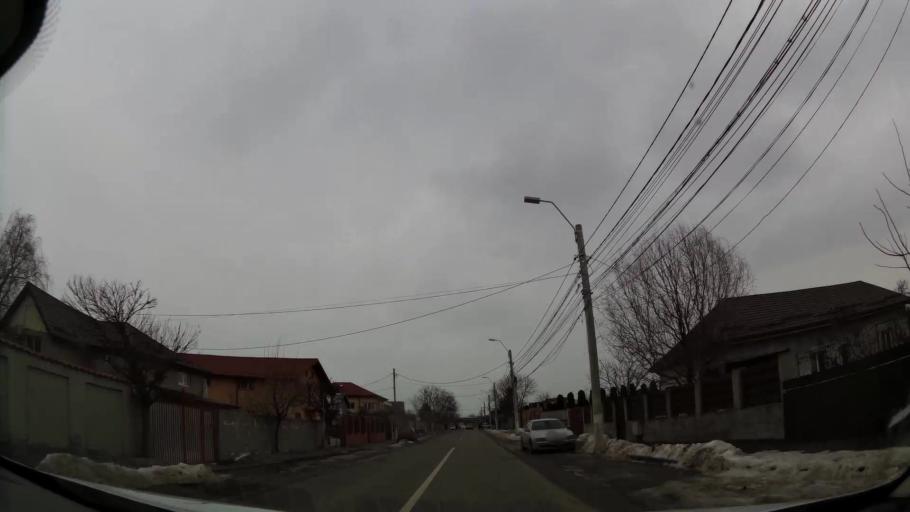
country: RO
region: Ilfov
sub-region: Comuna Tunari
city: Tunari
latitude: 44.5495
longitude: 26.1363
